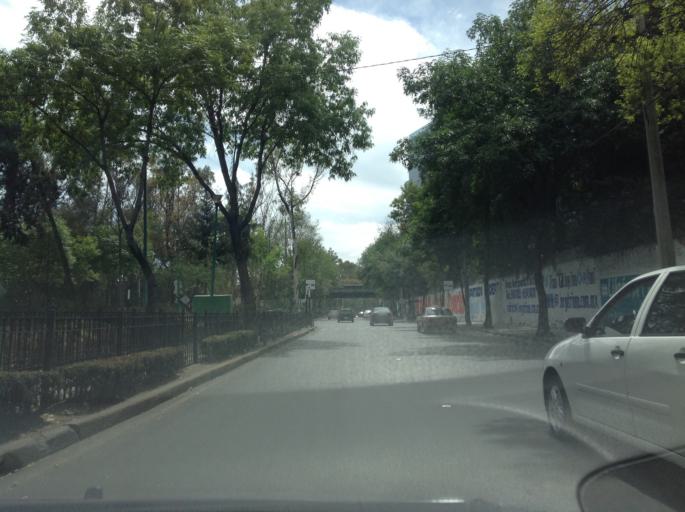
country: MX
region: Mexico City
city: Miguel Hidalgo
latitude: 19.4490
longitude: -99.2048
